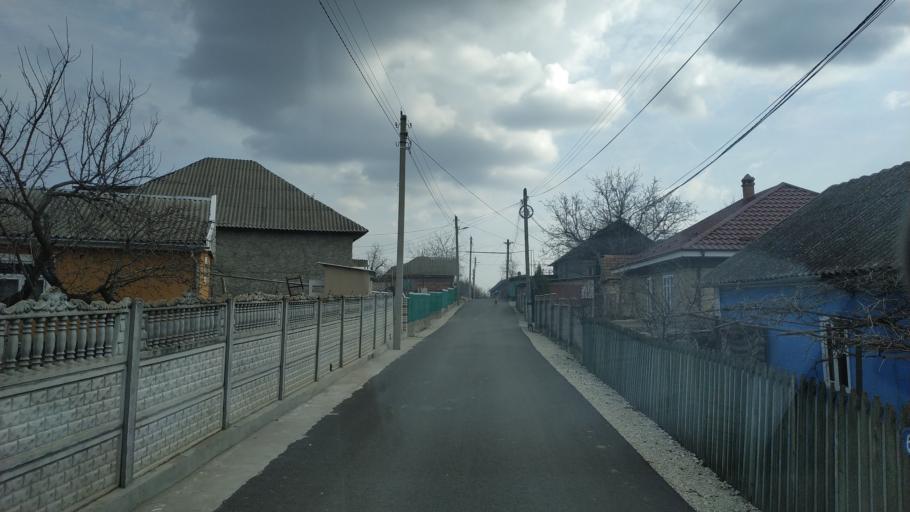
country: MD
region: Anenii Noi
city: Anenii Noi
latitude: 46.9004
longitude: 29.1410
